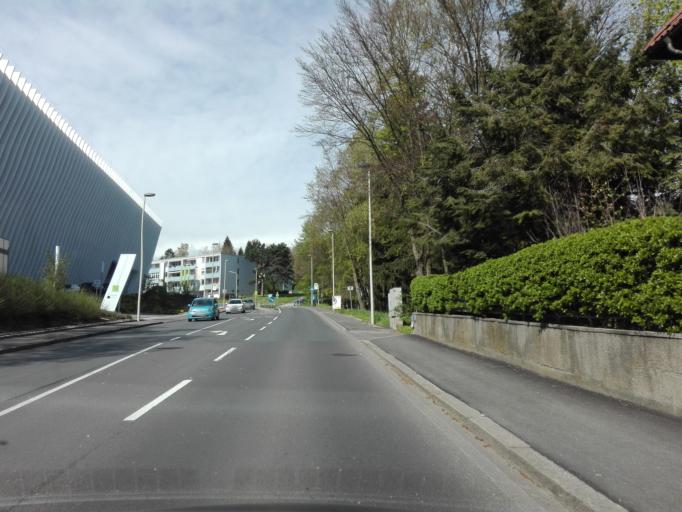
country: AT
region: Upper Austria
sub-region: Linz Stadt
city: Linz
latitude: 48.3114
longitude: 14.2704
